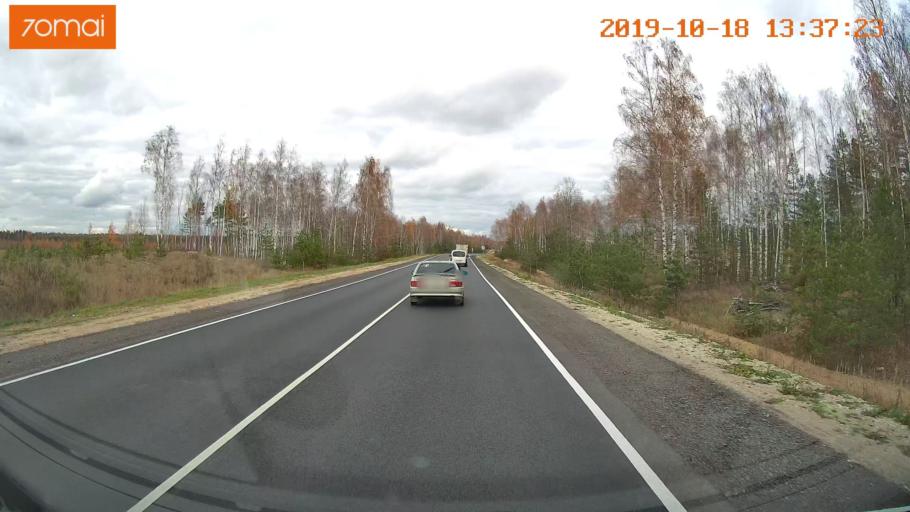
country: RU
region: Rjazan
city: Solotcha
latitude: 54.8788
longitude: 39.9950
